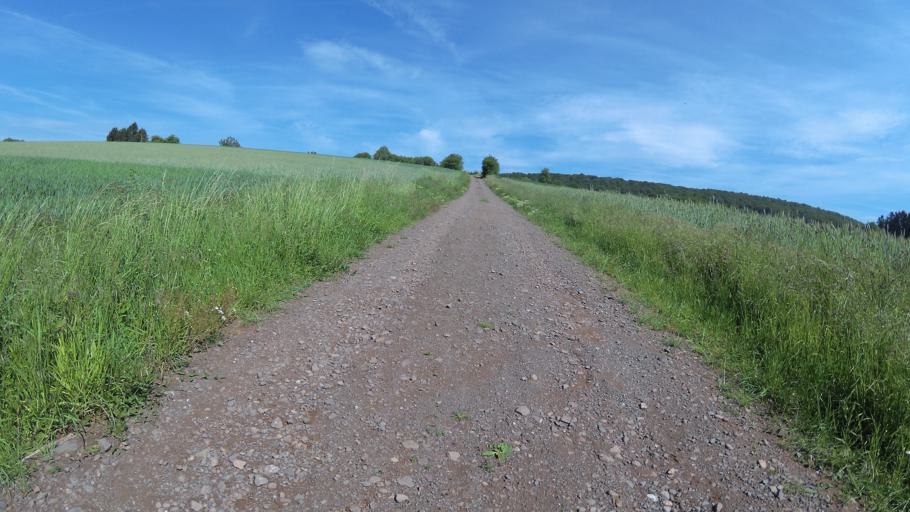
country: DE
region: Saarland
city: Ottweiler
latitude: 49.4317
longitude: 7.1720
